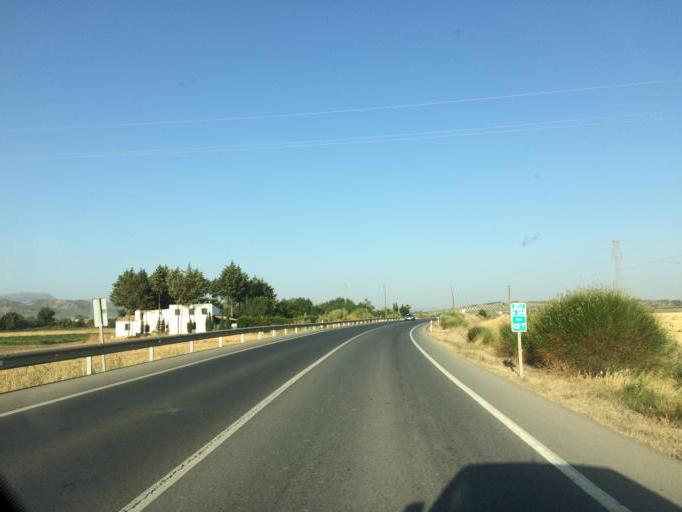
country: ES
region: Andalusia
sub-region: Provincia de Malaga
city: Mollina
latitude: 37.0530
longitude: -4.6427
